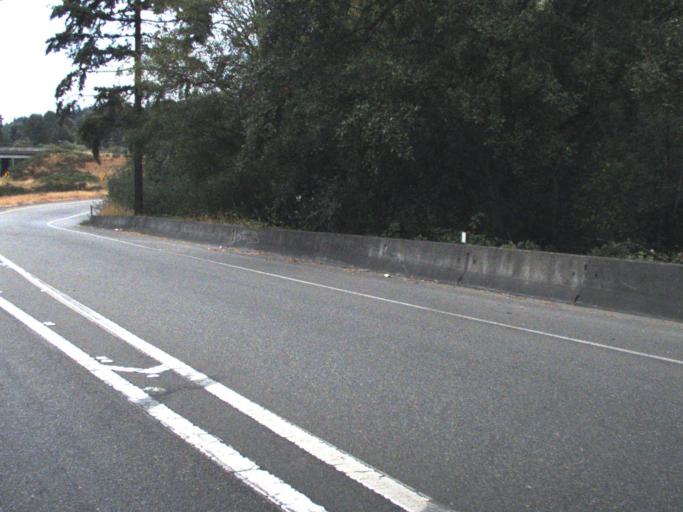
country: US
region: Washington
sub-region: King County
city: Newcastle
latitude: 47.5298
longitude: -122.1977
